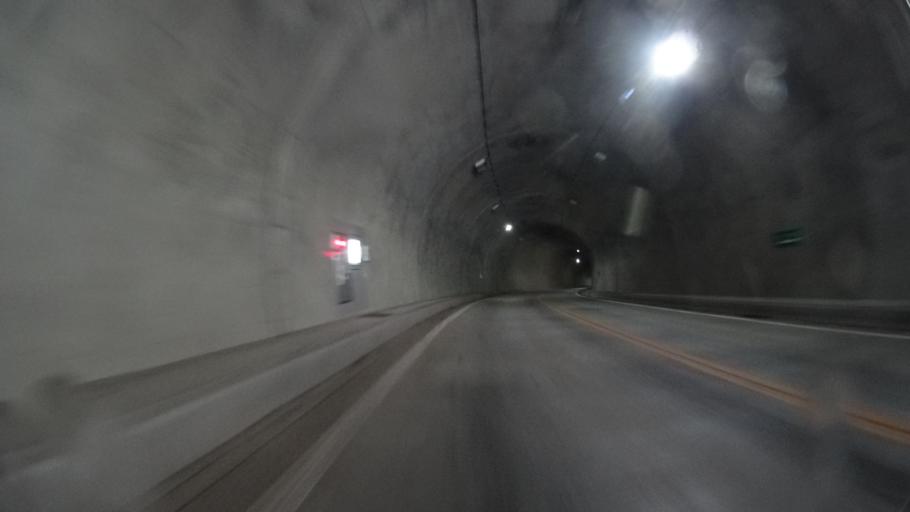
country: JP
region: Yamanashi
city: Enzan
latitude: 35.8056
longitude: 138.8643
